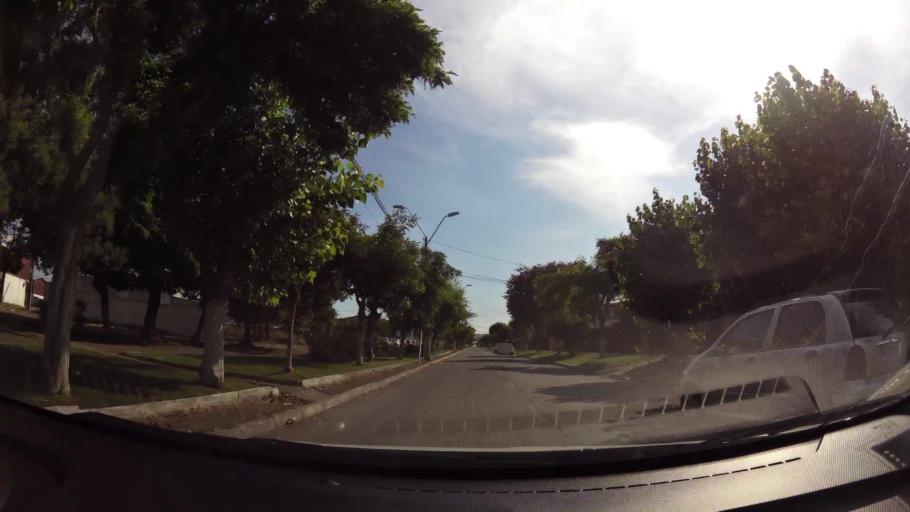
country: CL
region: Biobio
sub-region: Provincia de Concepcion
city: Talcahuano
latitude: -36.7890
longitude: -73.1080
